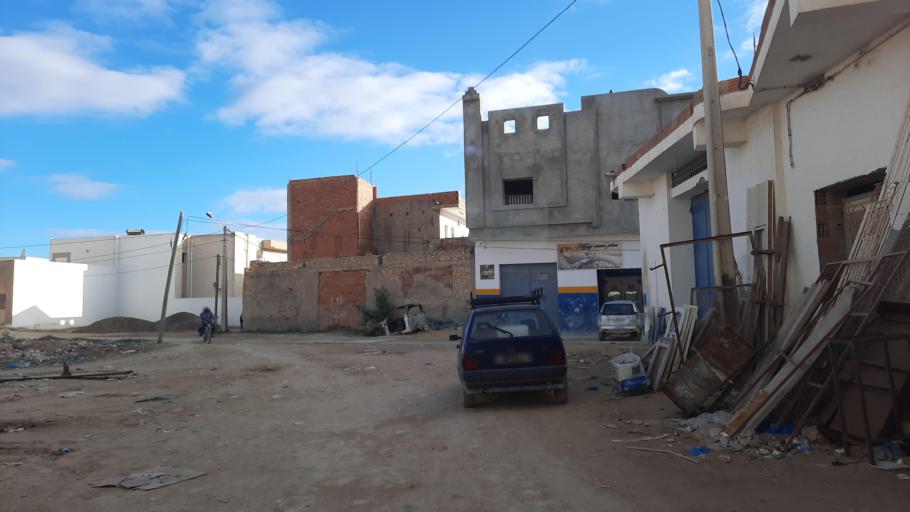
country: TN
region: Al Mahdiyah
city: El Jem
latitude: 35.2917
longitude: 10.7035
